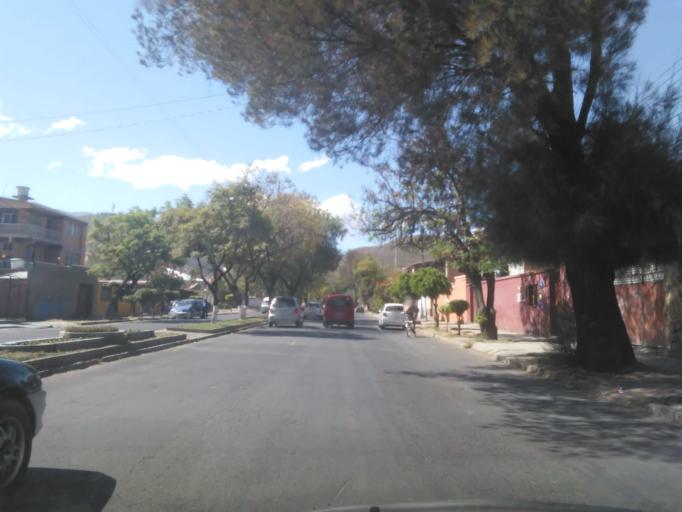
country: BO
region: Cochabamba
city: Cochabamba
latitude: -17.3977
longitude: -66.1465
